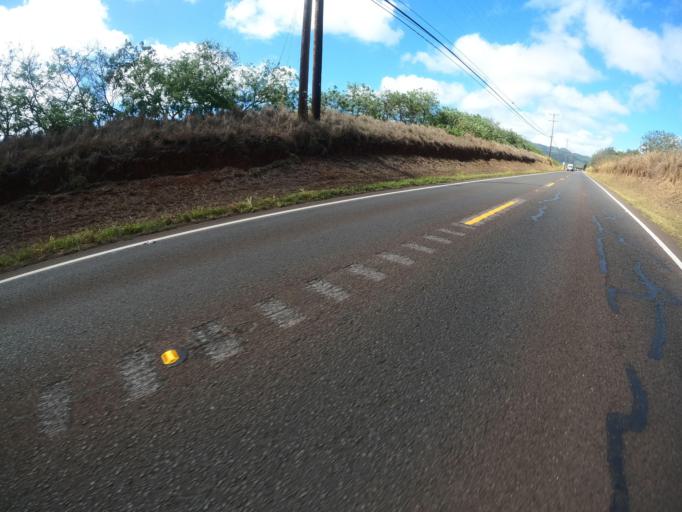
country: US
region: Hawaii
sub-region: Honolulu County
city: Village Park
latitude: 21.4219
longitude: -158.0510
